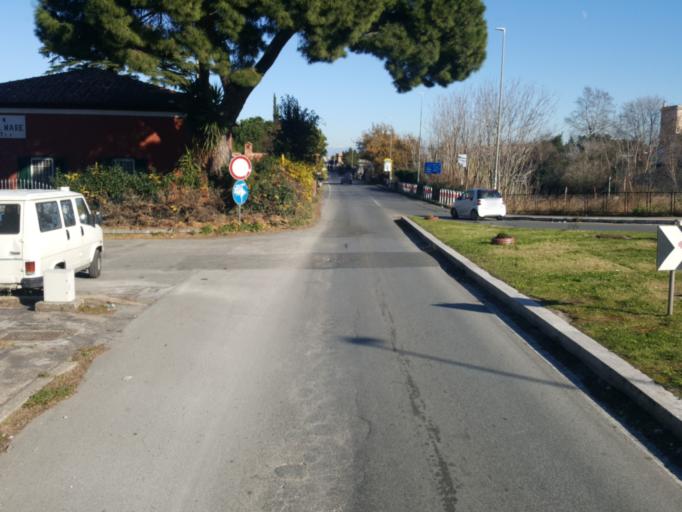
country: IT
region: Latium
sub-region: Citta metropolitana di Roma Capitale
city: Acilia-Castel Fusano-Ostia Antica
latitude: 41.7849
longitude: 12.3638
